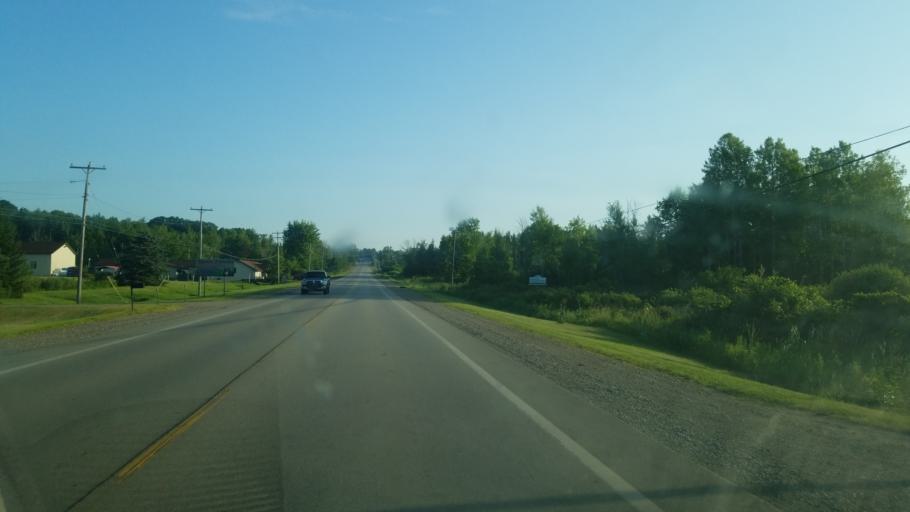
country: US
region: Michigan
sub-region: Montcalm County
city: Stanton
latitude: 43.2836
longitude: -85.0739
